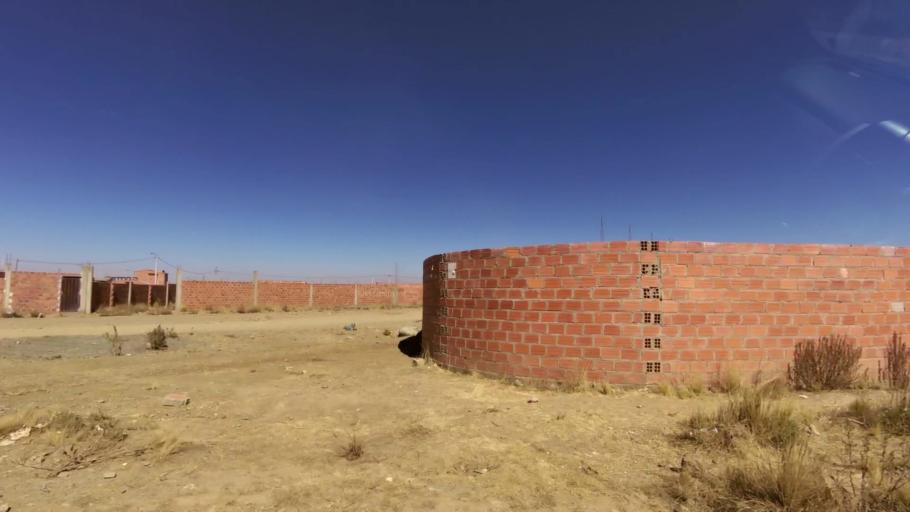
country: BO
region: La Paz
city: La Paz
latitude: -16.5770
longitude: -68.2177
